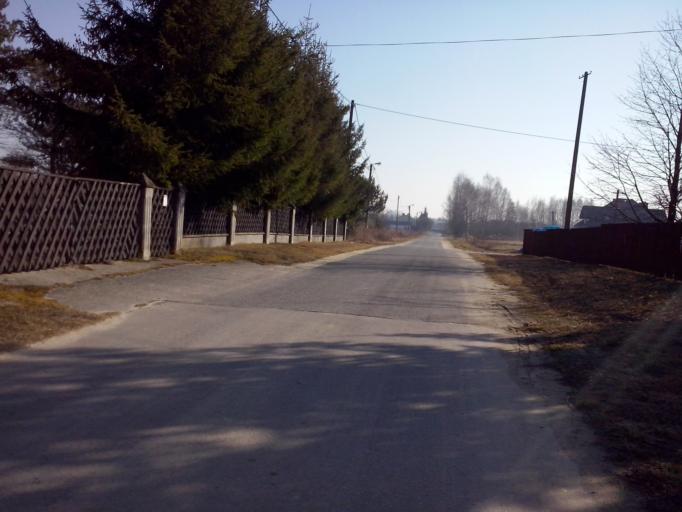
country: PL
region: Subcarpathian Voivodeship
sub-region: Powiat nizanski
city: Krzeszow
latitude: 50.4198
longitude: 22.3467
